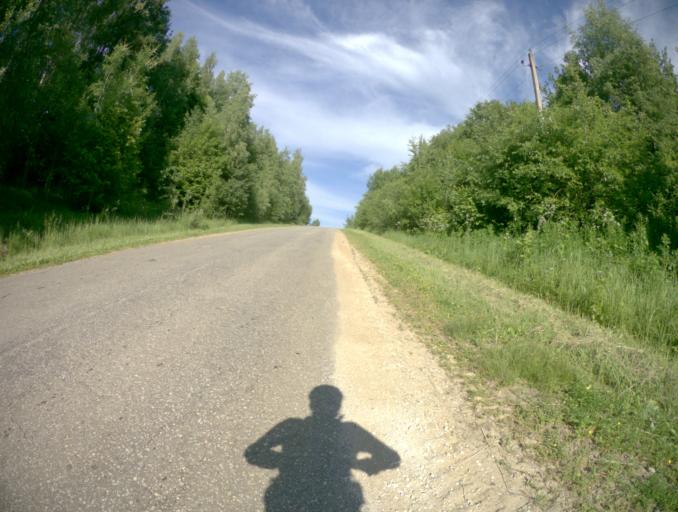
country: RU
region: Vladimir
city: Stavrovo
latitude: 56.1558
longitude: 40.1064
